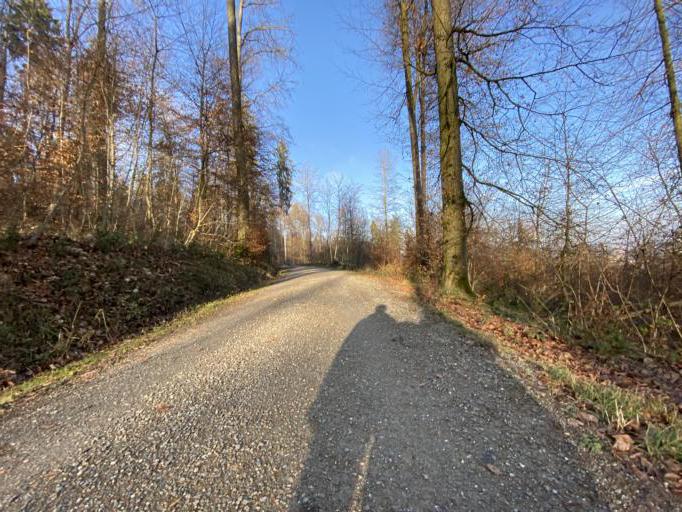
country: CH
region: Zurich
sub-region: Bezirk Winterthur
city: Toess (Kreis 4) / Vorder-Daettnau
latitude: 47.4874
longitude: 8.6990
